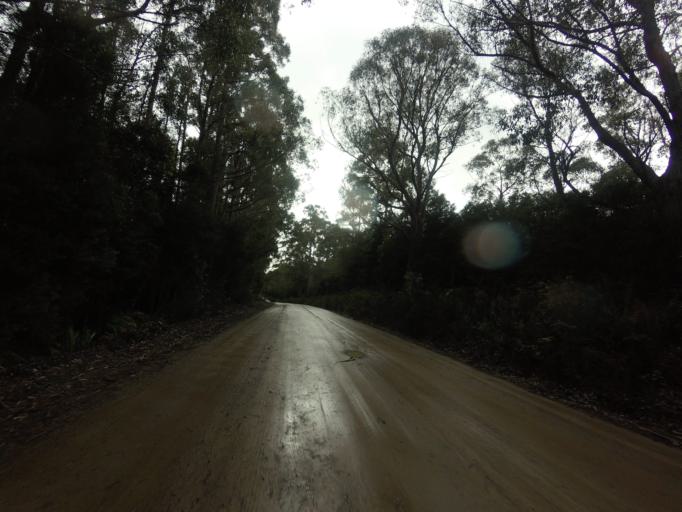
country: AU
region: Tasmania
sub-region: Huon Valley
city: Geeveston
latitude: -43.4575
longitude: 146.9022
